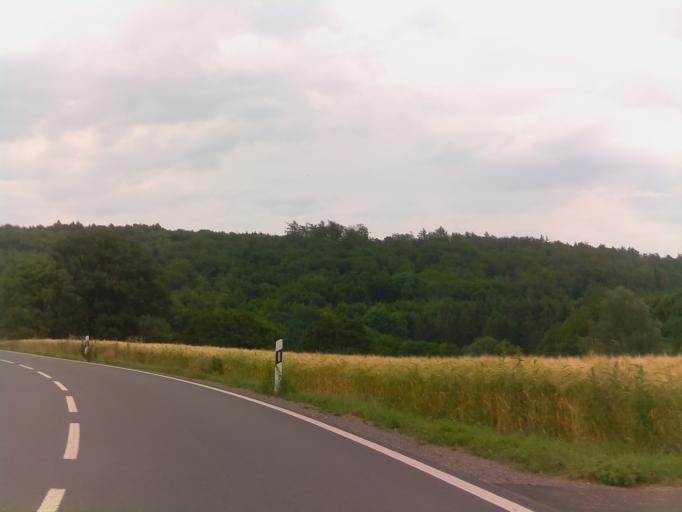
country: DE
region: North Rhine-Westphalia
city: Brakel
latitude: 51.7595
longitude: 9.1791
